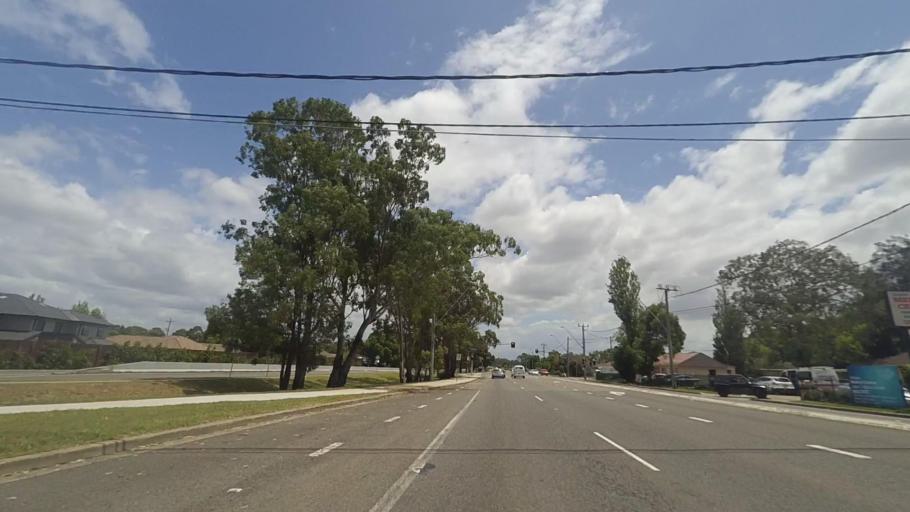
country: AU
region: New South Wales
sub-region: Bankstown
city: Milperra
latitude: -33.9500
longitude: 150.9507
